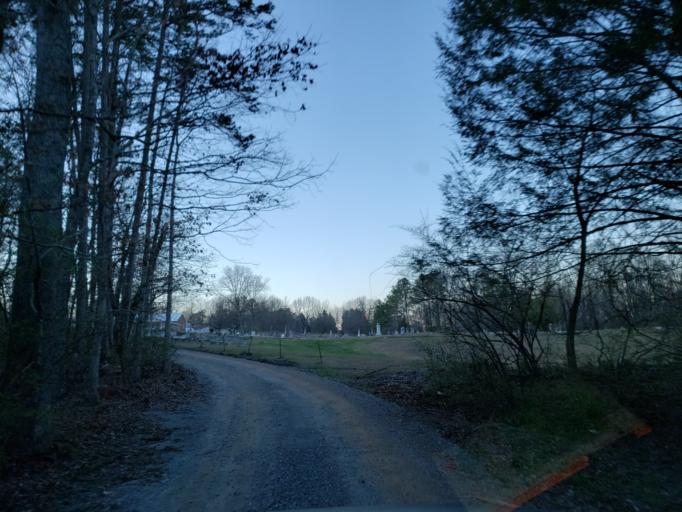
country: US
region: Georgia
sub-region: Pickens County
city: Nelson
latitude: 34.3763
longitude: -84.3624
